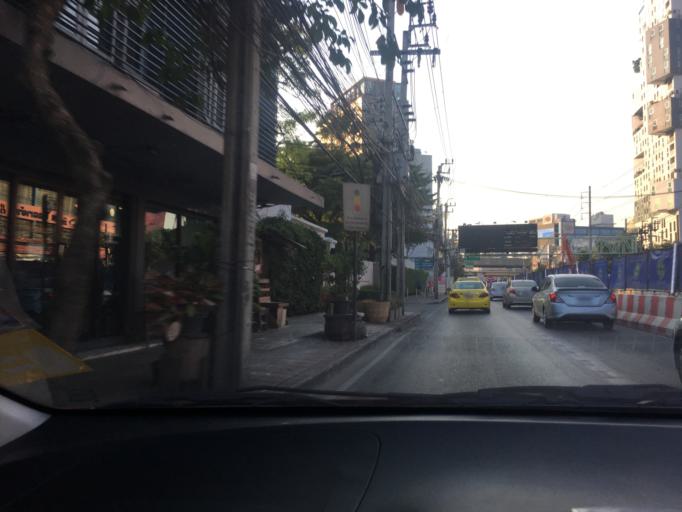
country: TH
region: Bangkok
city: Huai Khwang
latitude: 13.8042
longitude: 100.5770
